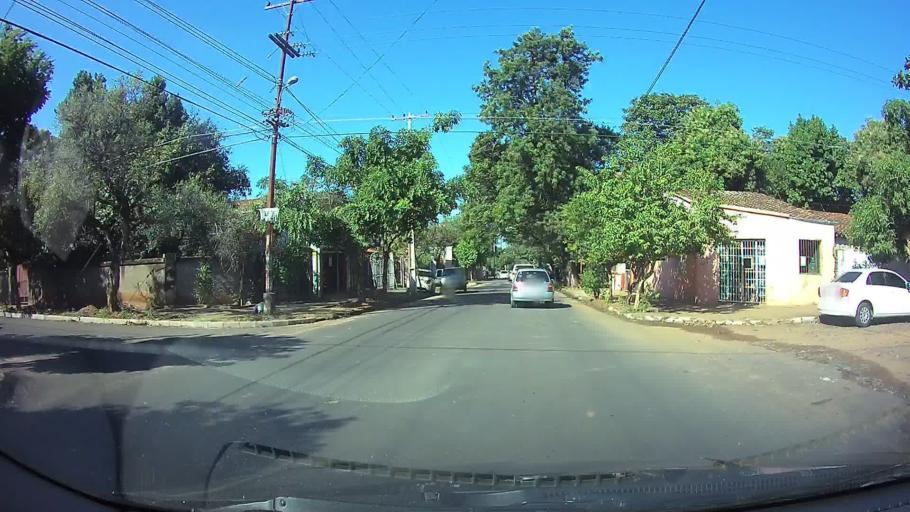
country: PY
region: Central
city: Lambare
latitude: -25.3202
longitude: -57.5741
